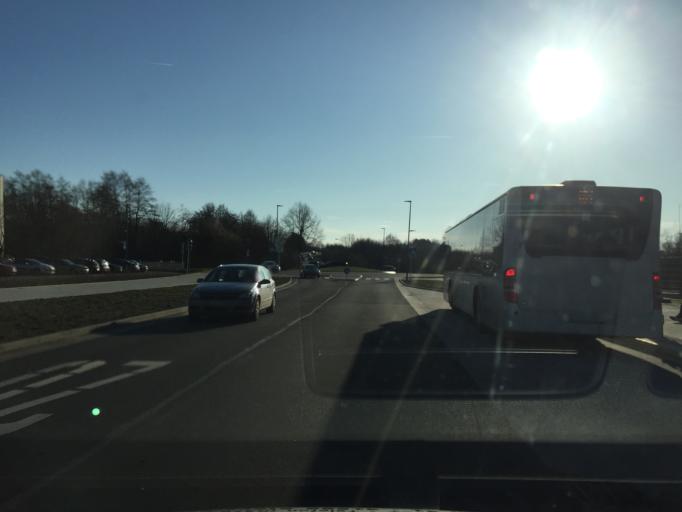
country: DE
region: Lower Saxony
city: Garbsen-Mitte
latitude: 52.4250
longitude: 9.6170
